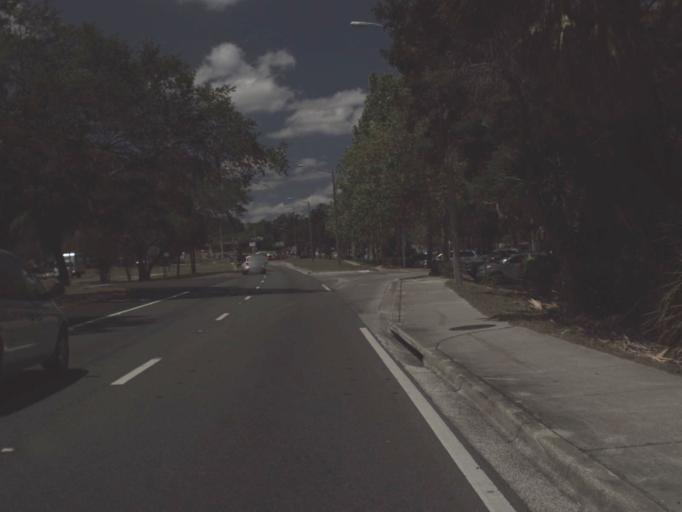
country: US
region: Florida
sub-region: Marion County
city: Ocala
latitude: 29.1894
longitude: -82.0998
